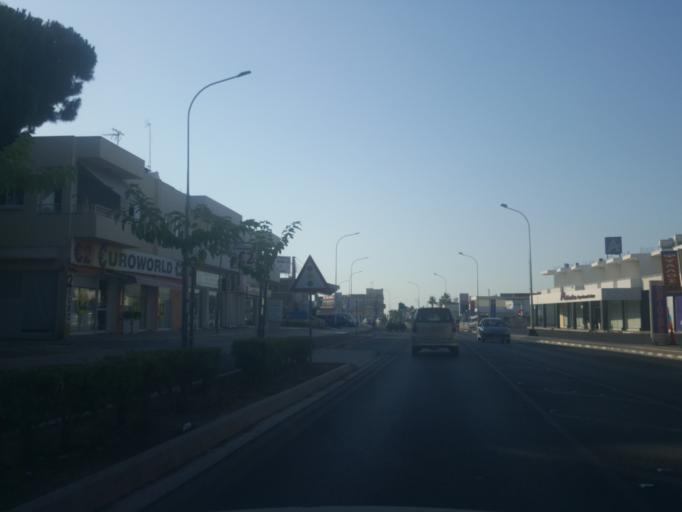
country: CY
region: Ammochostos
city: Deryneia
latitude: 35.0555
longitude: 33.9716
